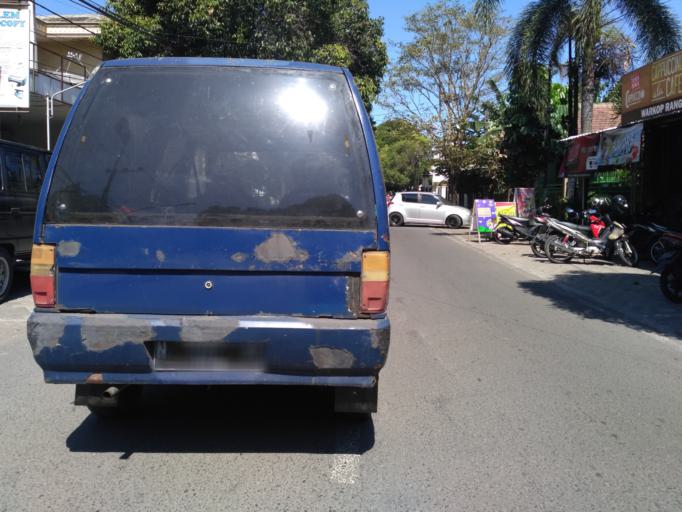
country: ID
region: East Java
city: Malang
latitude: -7.9731
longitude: 112.6668
